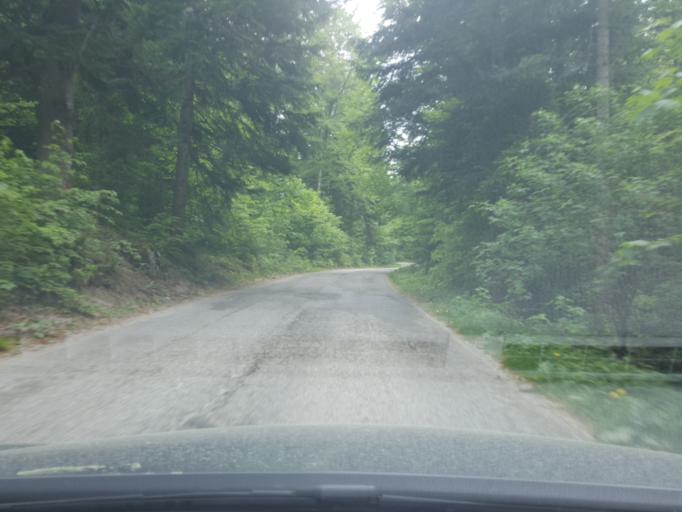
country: RS
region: Central Serbia
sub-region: Zlatiborski Okrug
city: Bajina Basta
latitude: 43.9234
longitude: 19.4838
